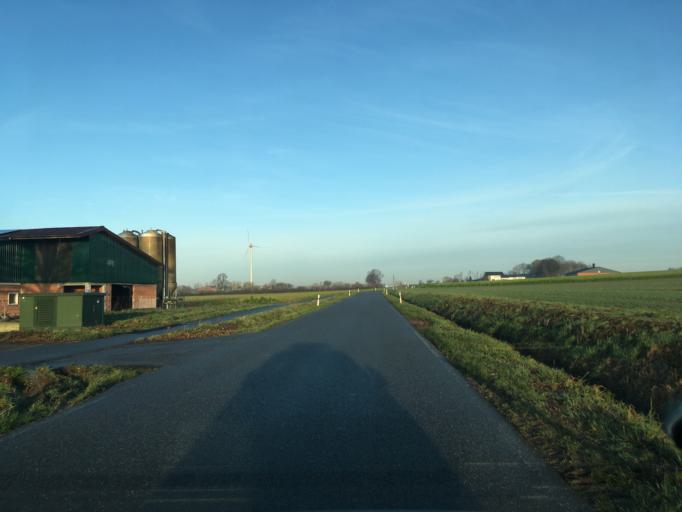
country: DE
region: North Rhine-Westphalia
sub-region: Regierungsbezirk Munster
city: Schoppingen
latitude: 52.0779
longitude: 7.2558
